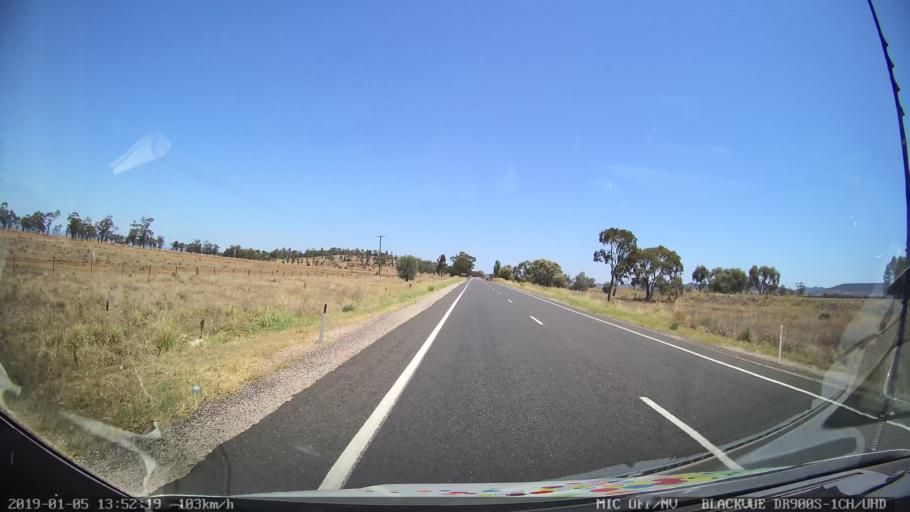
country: AU
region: New South Wales
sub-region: Gunnedah
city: Gunnedah
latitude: -31.0581
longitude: 150.2777
